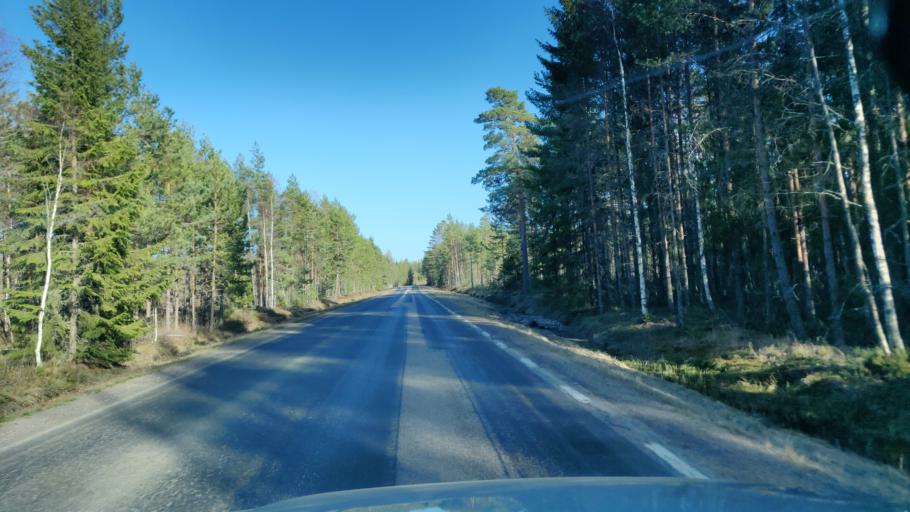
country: SE
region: Vaermland
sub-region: Sunne Kommun
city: Sunne
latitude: 59.9866
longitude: 13.3361
